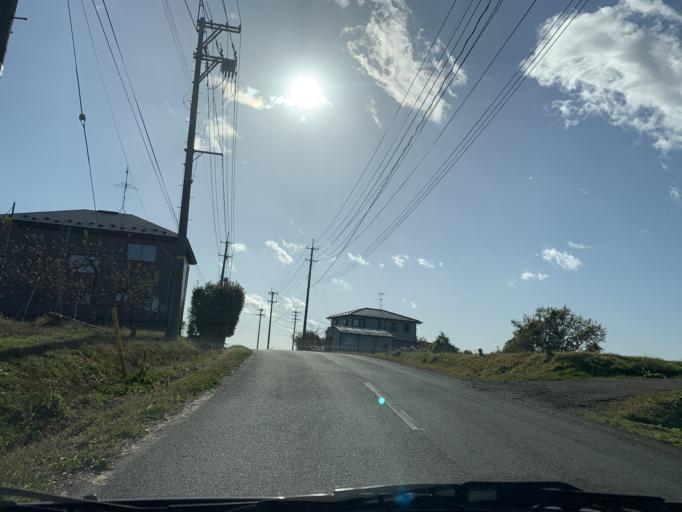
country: JP
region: Iwate
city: Mizusawa
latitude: 39.0600
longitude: 141.1183
